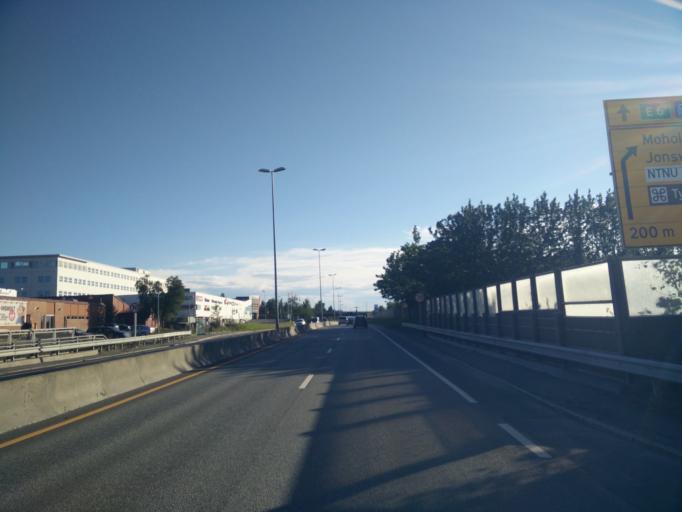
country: NO
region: Sor-Trondelag
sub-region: Trondheim
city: Trondheim
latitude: 63.4113
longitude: 10.4453
